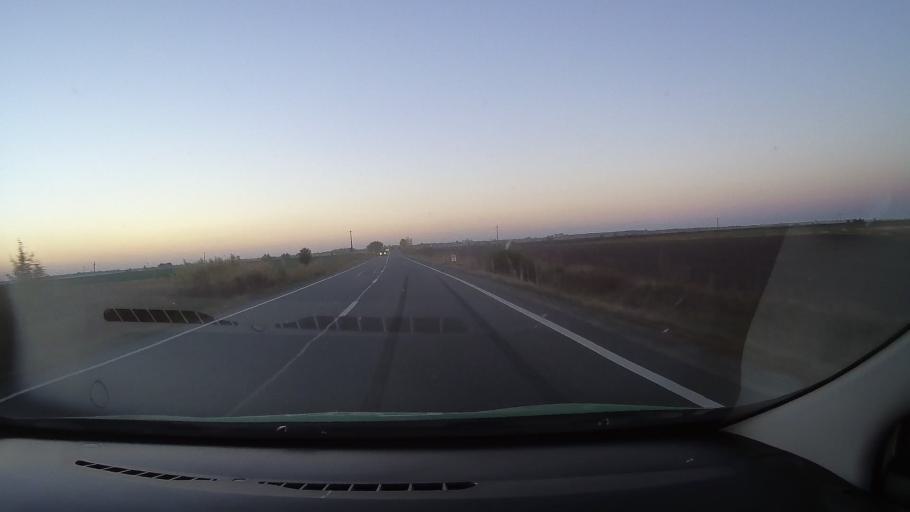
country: RO
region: Bihor
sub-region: Comuna Tarcea
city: Tarcea
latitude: 47.4433
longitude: 22.1900
